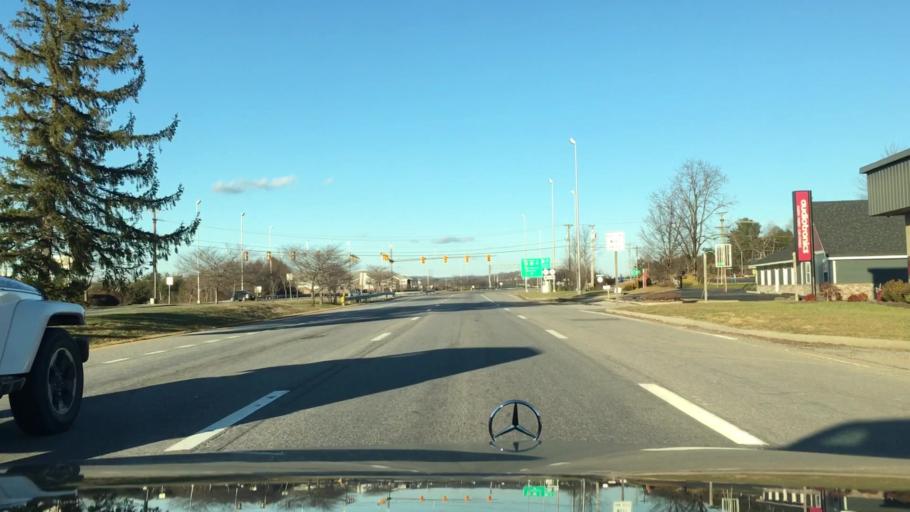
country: US
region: Virginia
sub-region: Montgomery County
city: Merrimac
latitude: 37.1868
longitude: -80.4075
